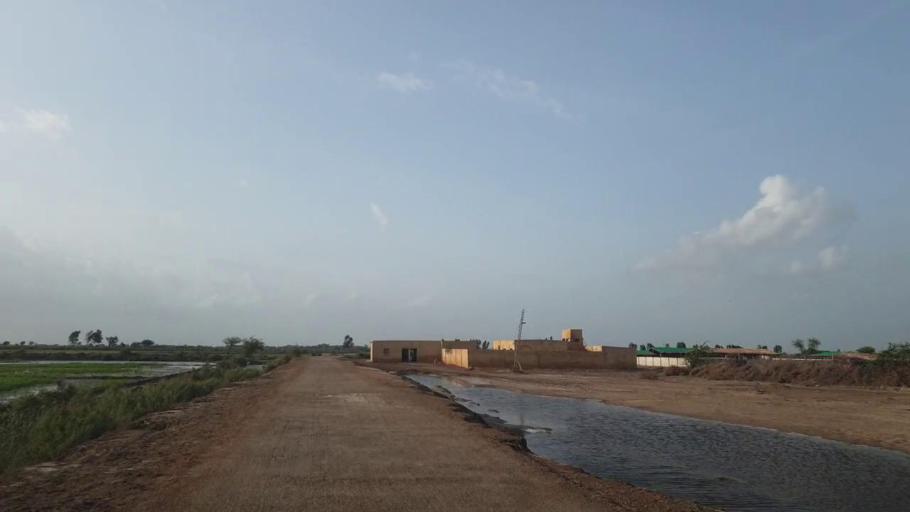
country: PK
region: Sindh
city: Tando Bago
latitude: 24.6612
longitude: 69.1120
